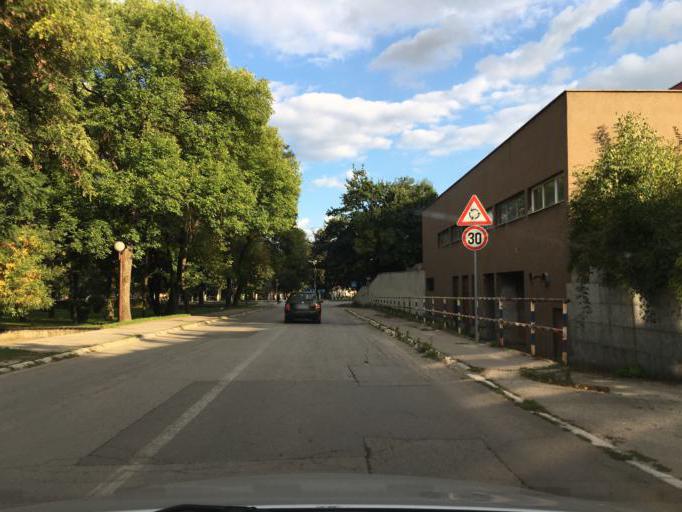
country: BA
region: Federation of Bosnia and Herzegovina
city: Bugojno
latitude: 44.0570
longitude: 17.4473
